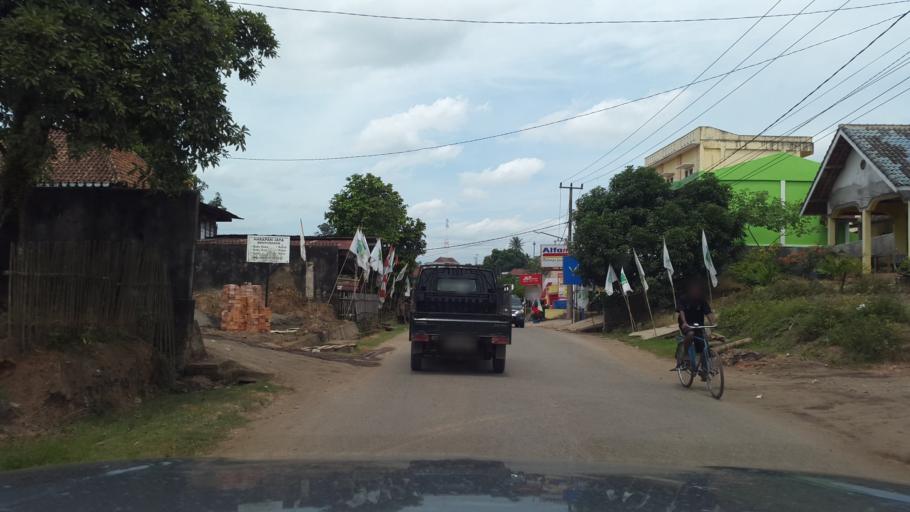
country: ID
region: South Sumatra
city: Gunungmegang Dalam
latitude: -3.2825
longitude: 103.8323
